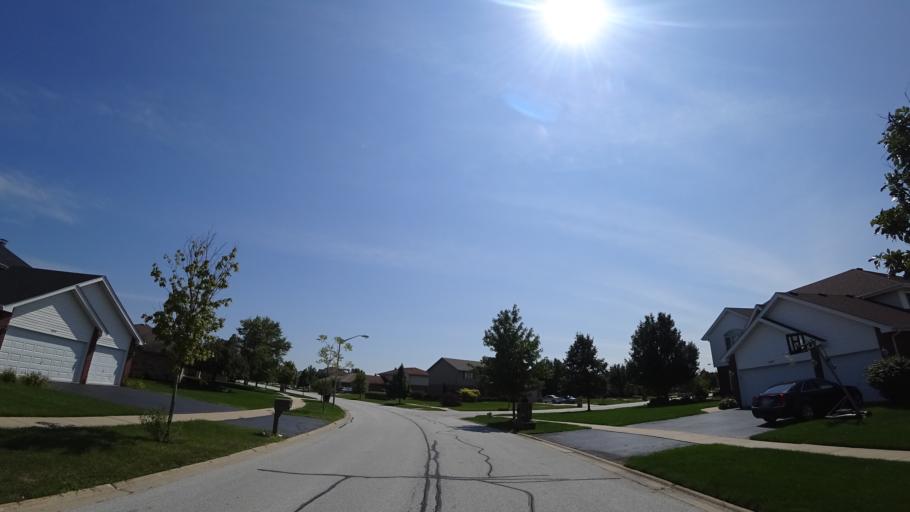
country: US
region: Illinois
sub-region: Cook County
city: Orland Hills
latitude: 41.5626
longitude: -87.8271
